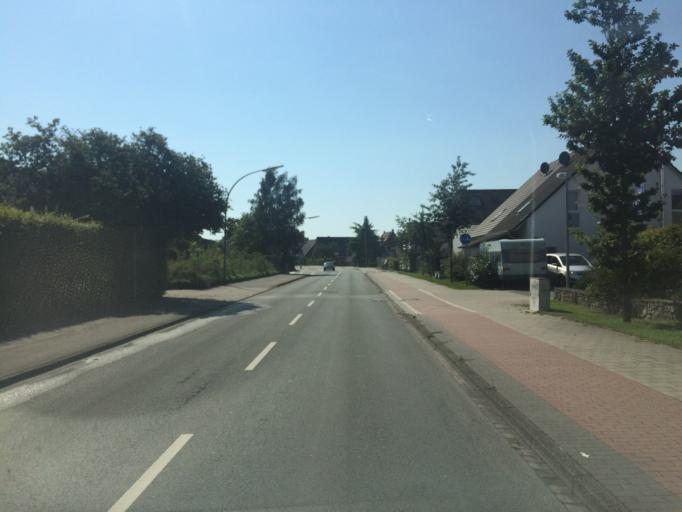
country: DE
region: North Rhine-Westphalia
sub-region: Regierungsbezirk Munster
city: Telgte
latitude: 52.0000
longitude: 7.7097
